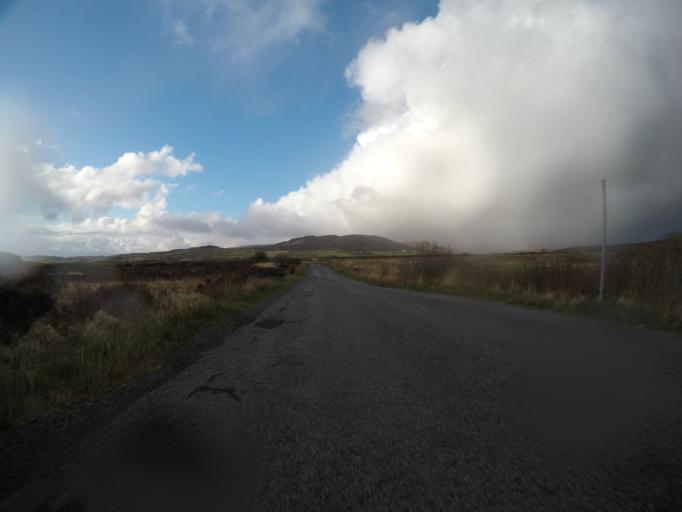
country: GB
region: Scotland
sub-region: Highland
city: Portree
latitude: 57.4718
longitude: -6.2985
